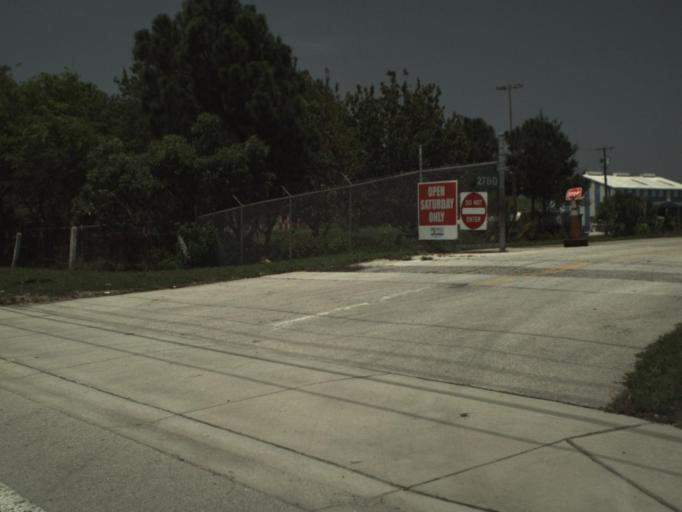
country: US
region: Florida
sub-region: Broward County
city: Kendall Green
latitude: 26.2649
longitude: -80.1518
